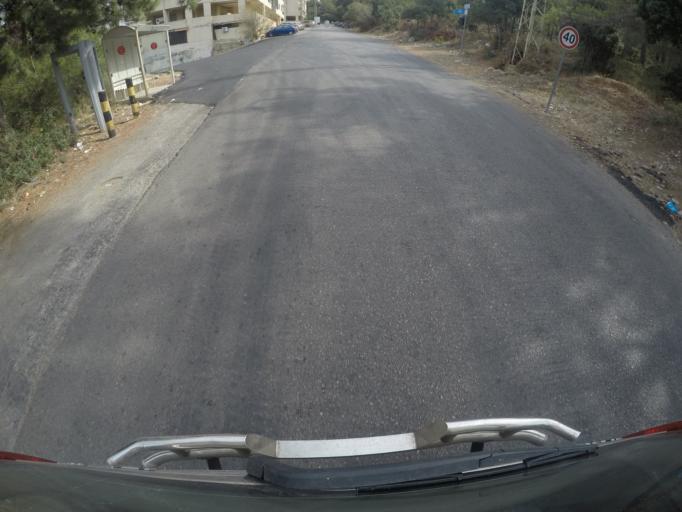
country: LB
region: Mont-Liban
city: Beit ed Dine
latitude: 33.7349
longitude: 35.4888
